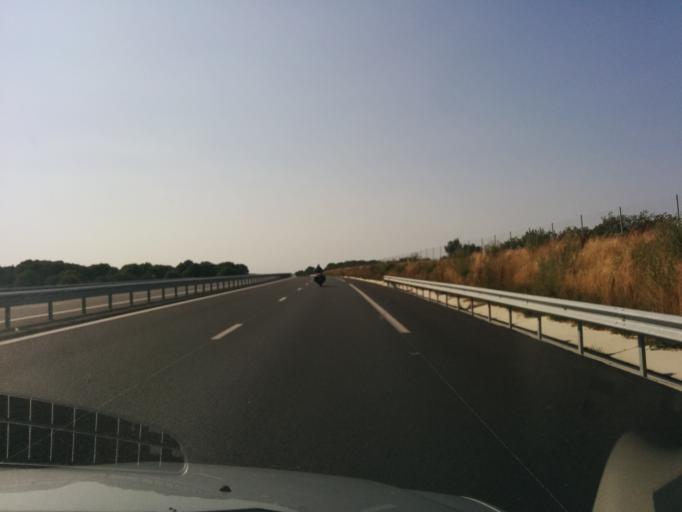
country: FR
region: Poitou-Charentes
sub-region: Departement des Deux-Sevres
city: Nueil-les-Aubiers
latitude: 46.8721
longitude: -0.5798
